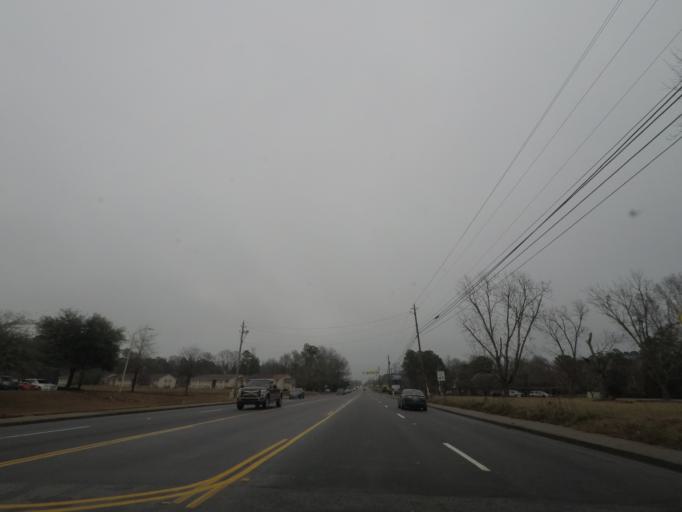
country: US
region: South Carolina
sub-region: Clarendon County
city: Manning
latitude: 33.6992
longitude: -80.2340
